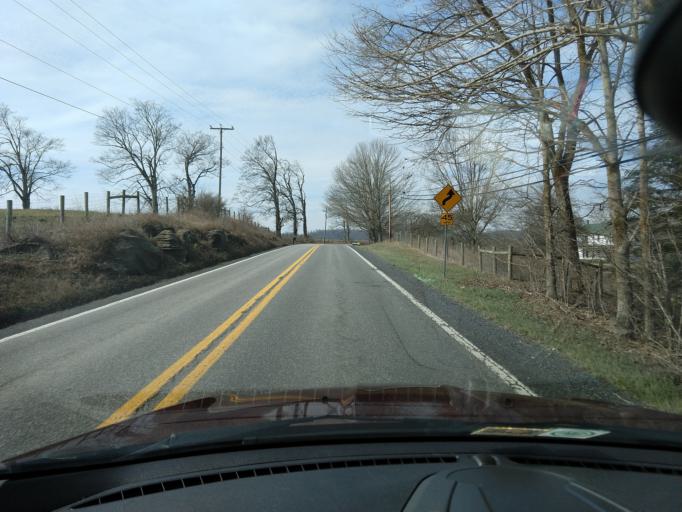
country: US
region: West Virginia
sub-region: Greenbrier County
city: Lewisburg
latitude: 37.9014
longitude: -80.3992
